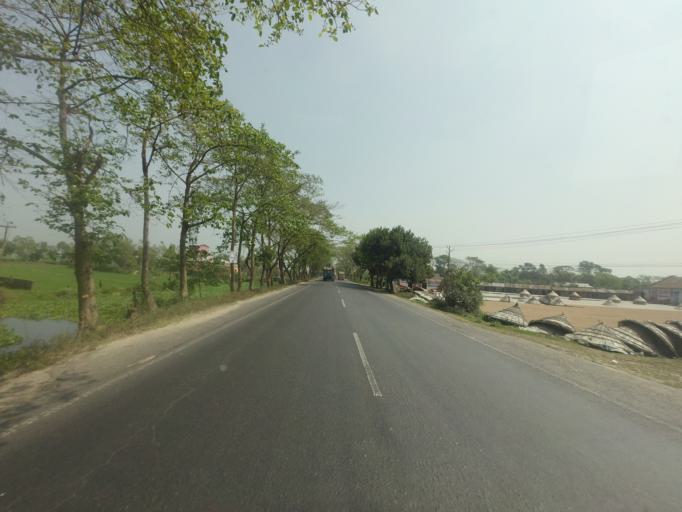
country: BD
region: Dhaka
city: Bhairab Bazar
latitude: 24.0477
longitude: 91.0920
